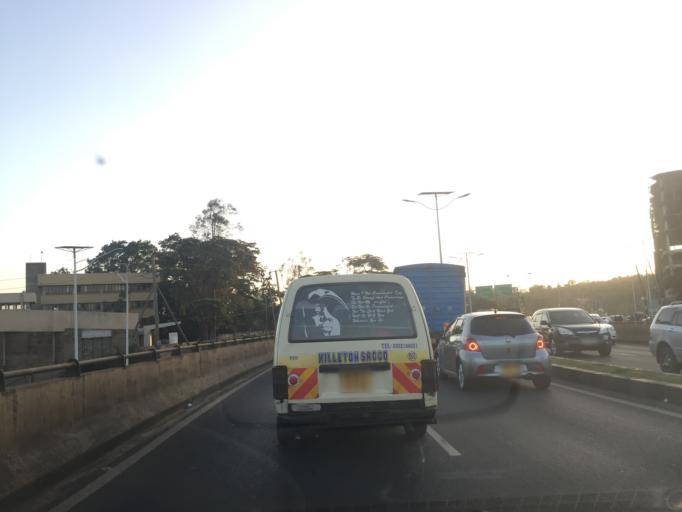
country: KE
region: Nairobi Area
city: Nairobi
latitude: -1.2722
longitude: 36.8145
